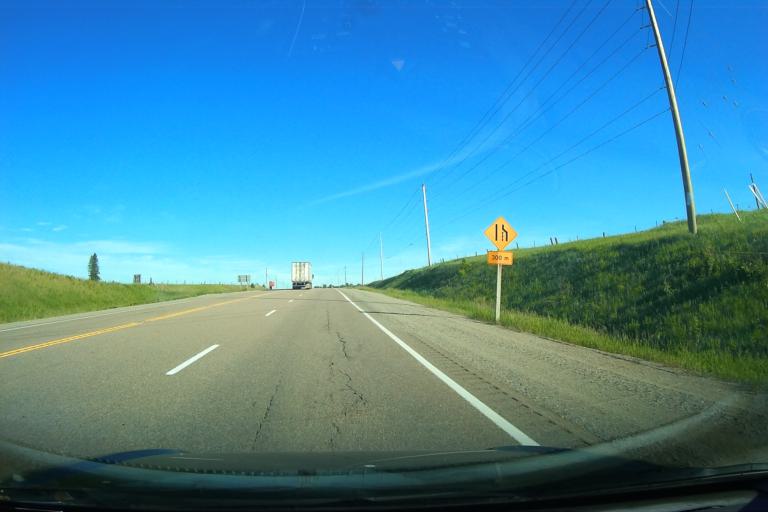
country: CA
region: Ontario
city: Renfrew
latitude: 45.6046
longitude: -76.8513
